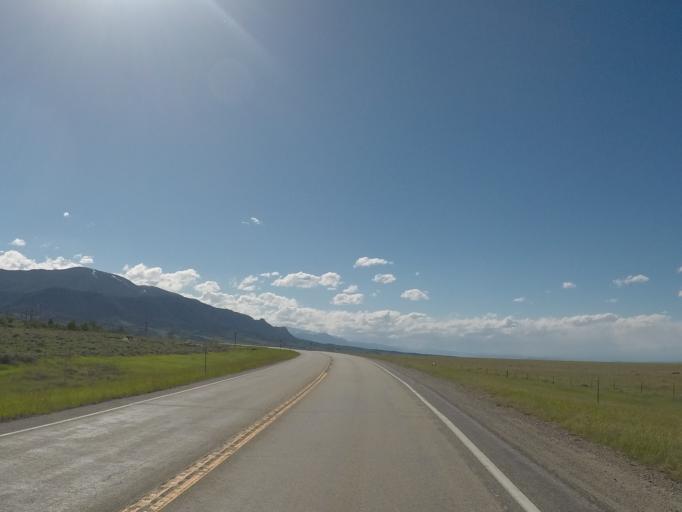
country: US
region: Montana
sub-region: Carbon County
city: Red Lodge
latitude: 45.1829
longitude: -109.2300
